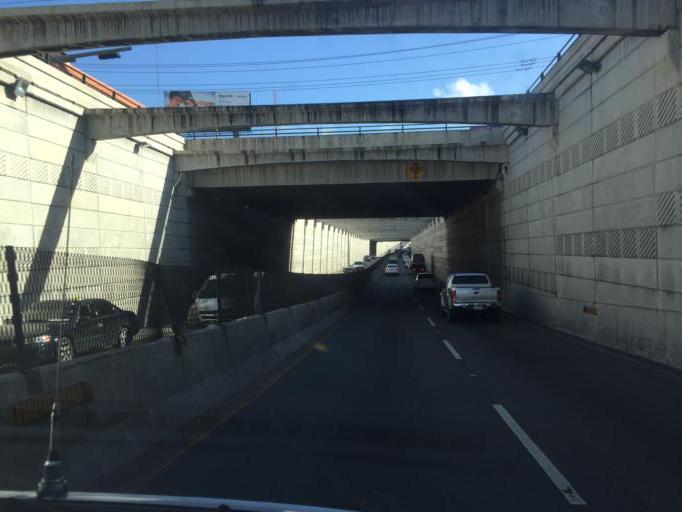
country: DO
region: Nacional
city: Bella Vista
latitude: 18.4569
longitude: -69.9499
